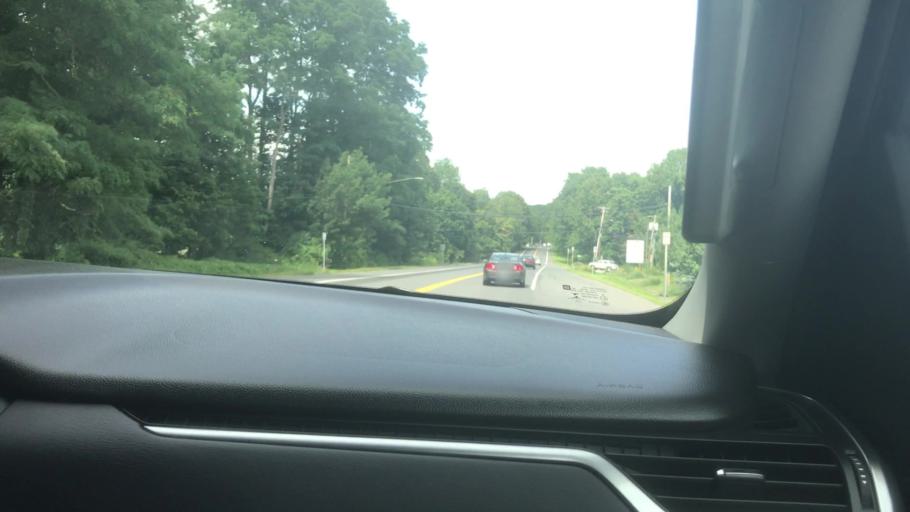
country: US
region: New York
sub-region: Dutchess County
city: Dover Plains
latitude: 41.8586
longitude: -73.5531
